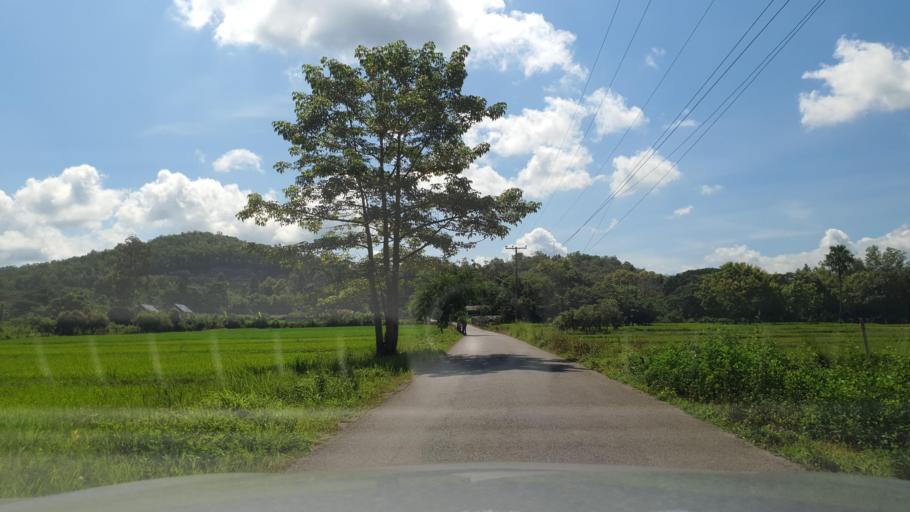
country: TH
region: Chiang Mai
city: San Kamphaeng
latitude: 18.7726
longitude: 99.1699
